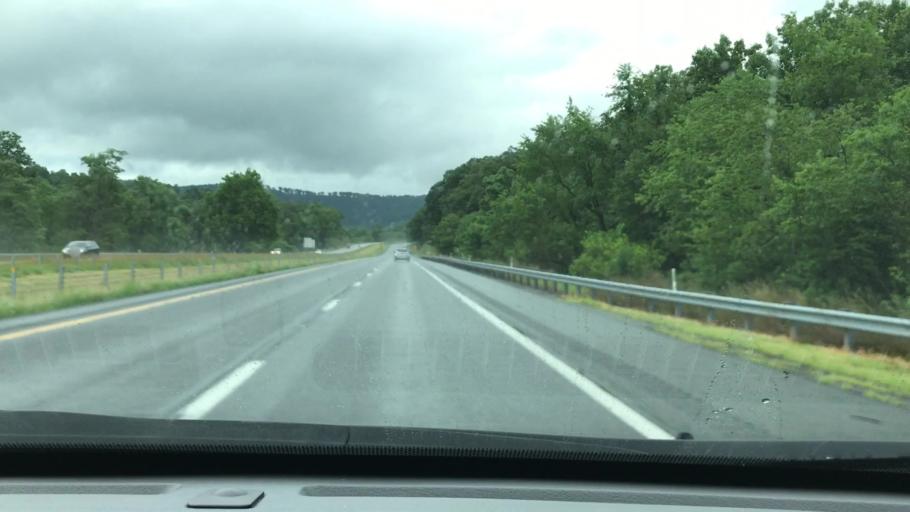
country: US
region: Maryland
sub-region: Washington County
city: Hancock
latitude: 39.8034
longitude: -78.2619
